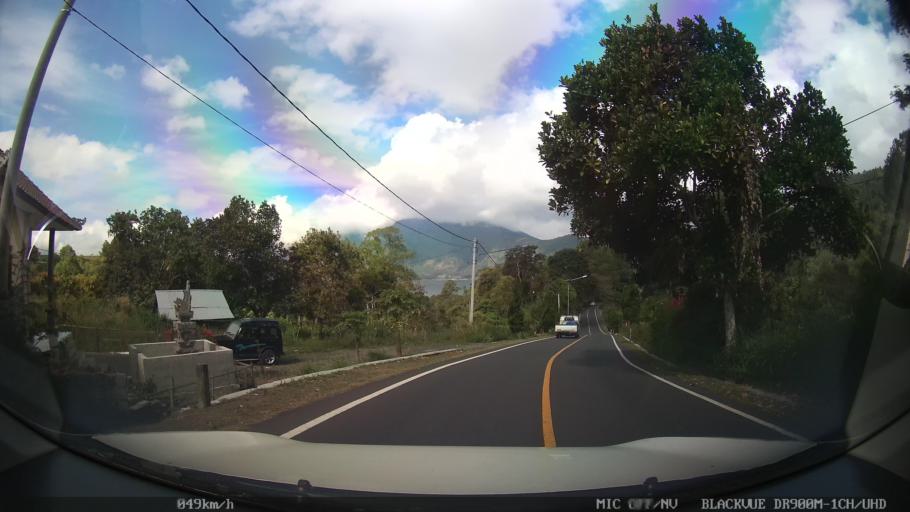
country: ID
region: Bali
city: Banjar Kedisan
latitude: -8.2772
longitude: 115.3724
